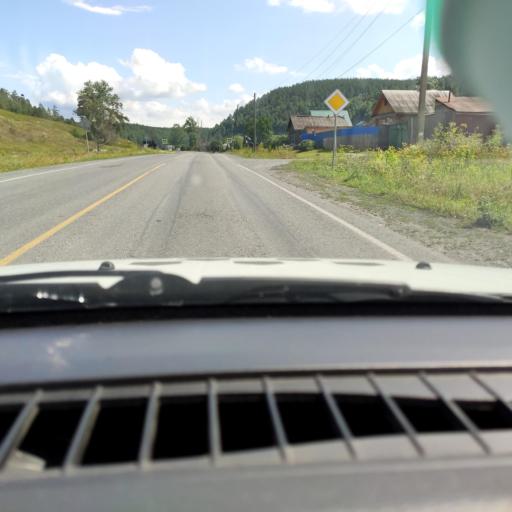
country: RU
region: Chelyabinsk
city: Mezhevoy
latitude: 55.1557
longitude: 58.8290
